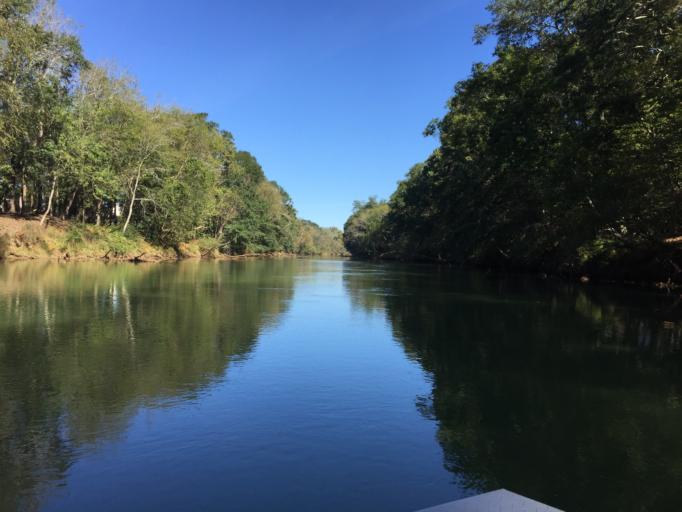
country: US
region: Georgia
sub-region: Gwinnett County
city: Berkeley Lake
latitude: 34.0008
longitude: -84.1799
